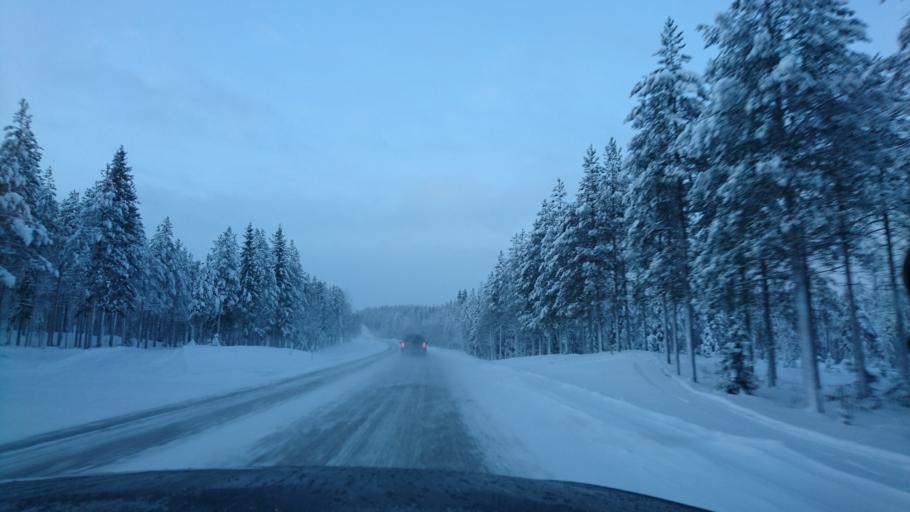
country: FI
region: Northern Ostrobothnia
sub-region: Koillismaa
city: Taivalkoski
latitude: 65.4689
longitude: 27.6972
